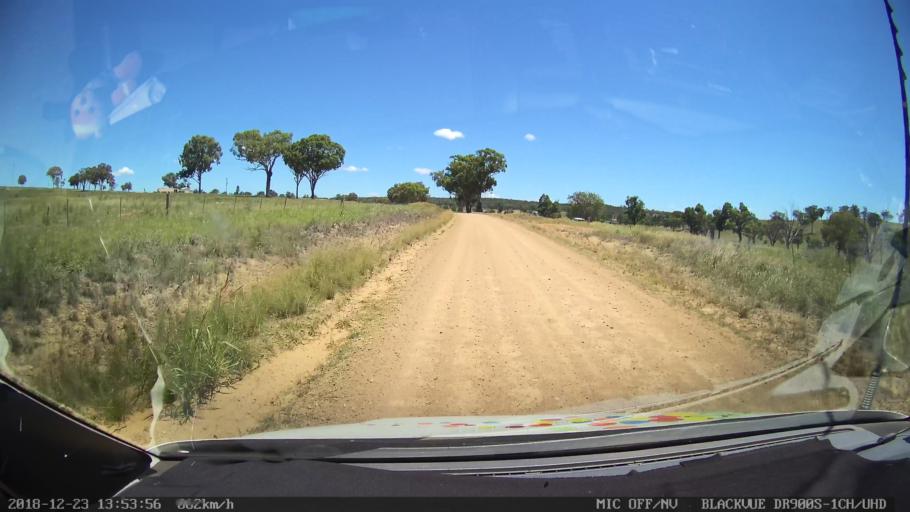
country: AU
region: New South Wales
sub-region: Tamworth Municipality
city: Manilla
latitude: -30.5564
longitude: 151.0918
